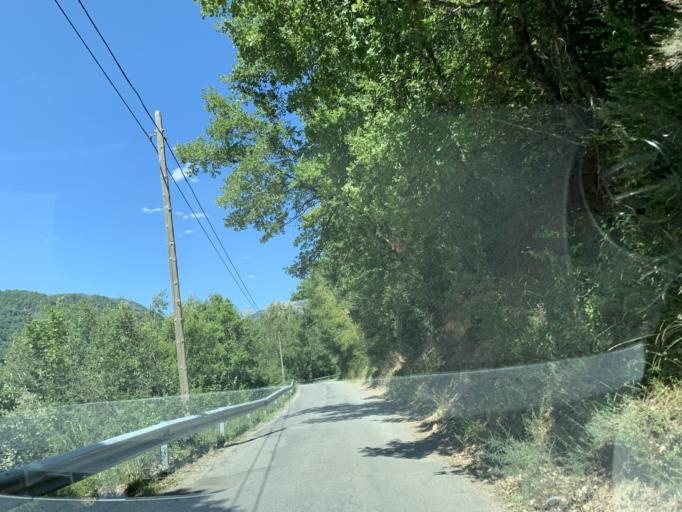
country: ES
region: Aragon
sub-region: Provincia de Huesca
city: Hoz de Jaca
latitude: 42.7090
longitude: -0.3037
